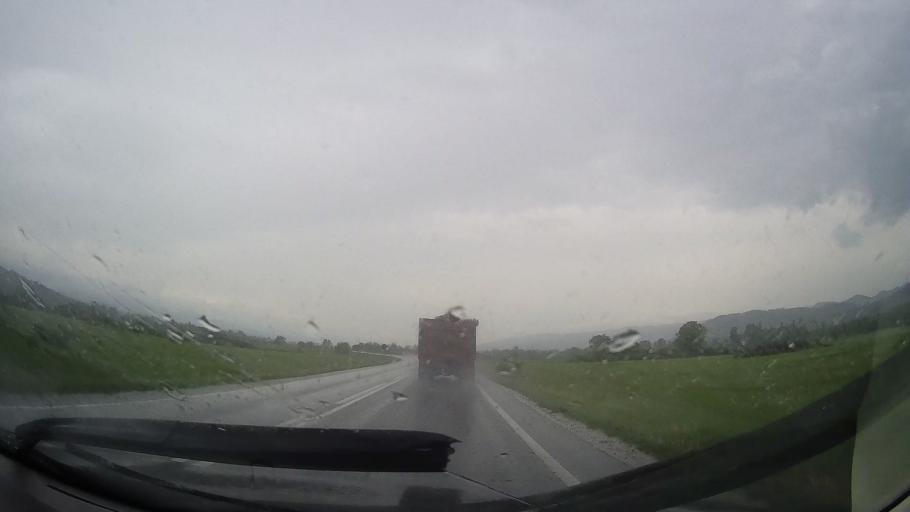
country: RO
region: Caras-Severin
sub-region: Comuna Bucosnita
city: Petrosnita
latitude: 45.3291
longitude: 22.2691
